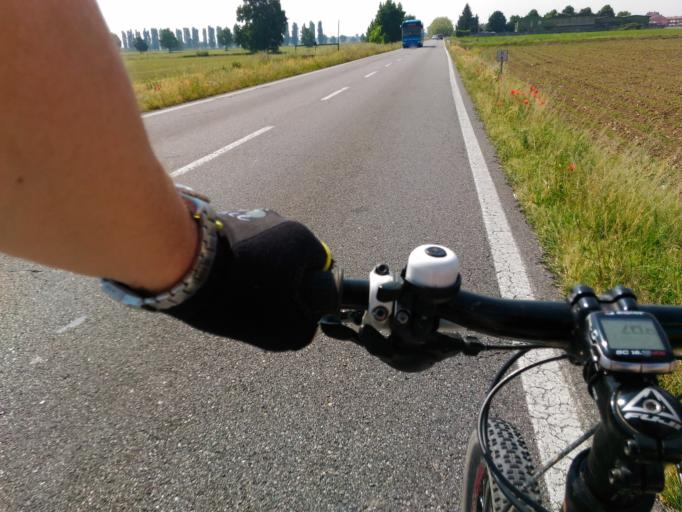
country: IT
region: Lombardy
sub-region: Provincia di Lodi
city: Salerano sul Lambro
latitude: 45.2774
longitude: 9.3822
